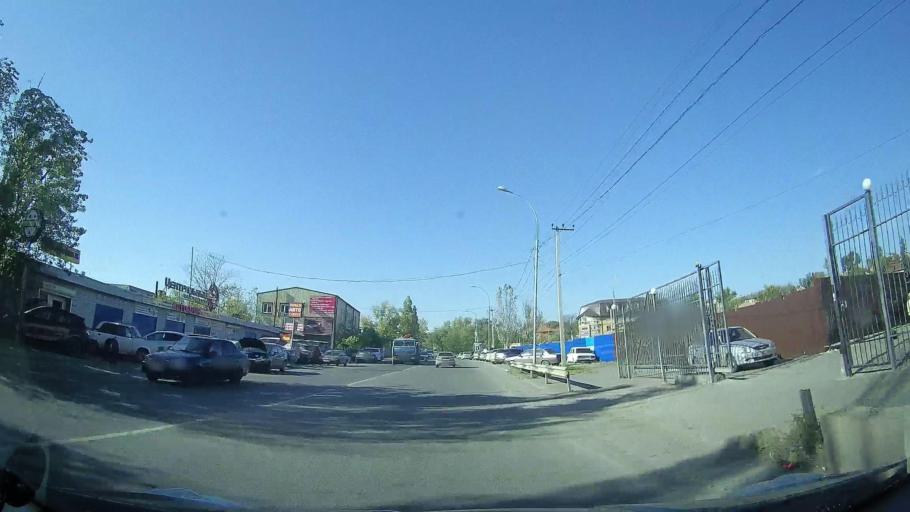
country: RU
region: Rostov
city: Rostov-na-Donu
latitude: 47.2246
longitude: 39.6858
